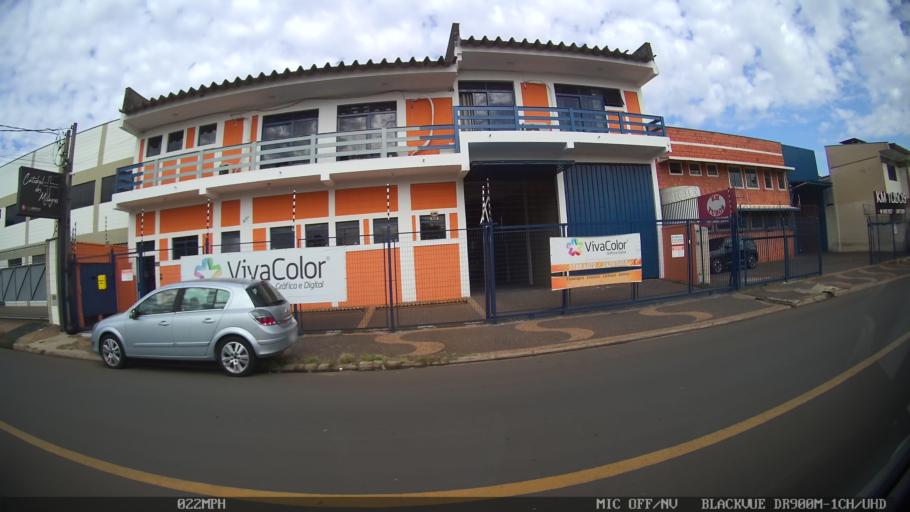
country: BR
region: Sao Paulo
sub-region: Americana
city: Americana
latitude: -22.7423
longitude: -47.3587
